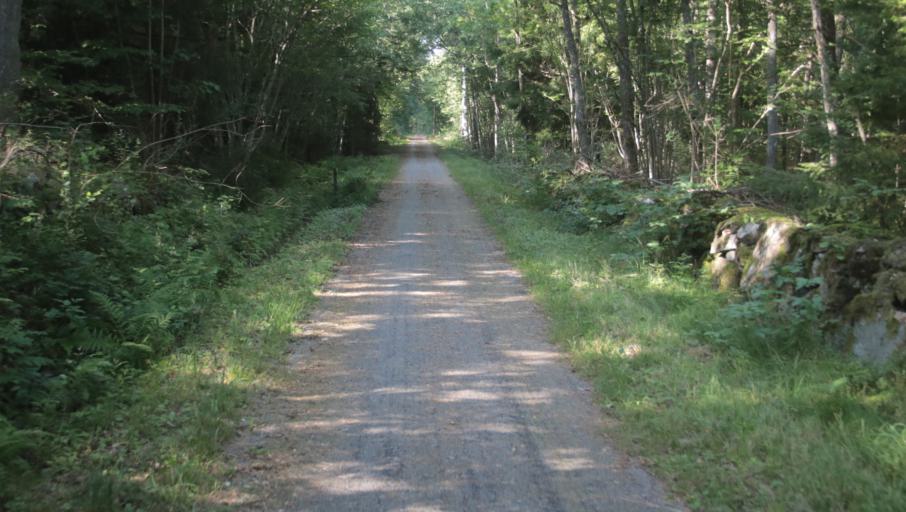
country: SE
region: Blekinge
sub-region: Karlshamns Kommun
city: Svangsta
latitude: 56.3838
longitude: 14.6773
